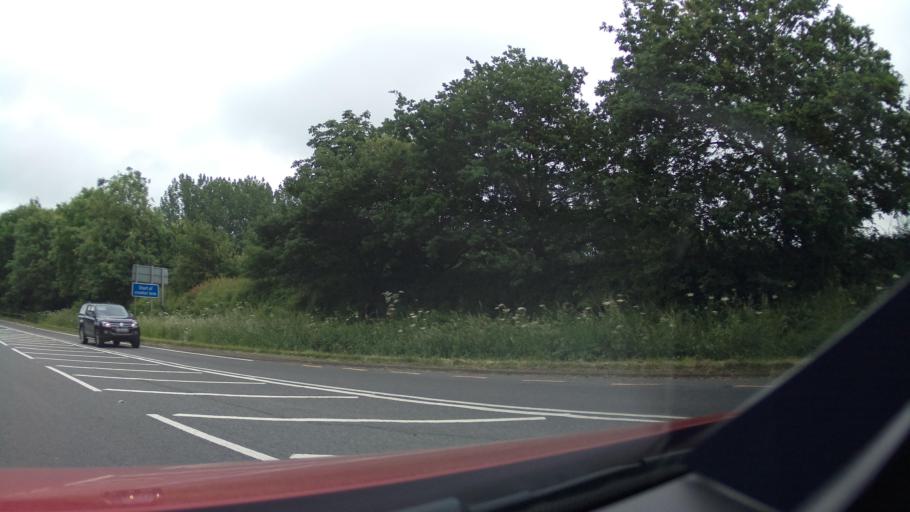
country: GB
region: England
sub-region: District of Rutland
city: Ridlington
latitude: 52.5951
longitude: -0.8472
